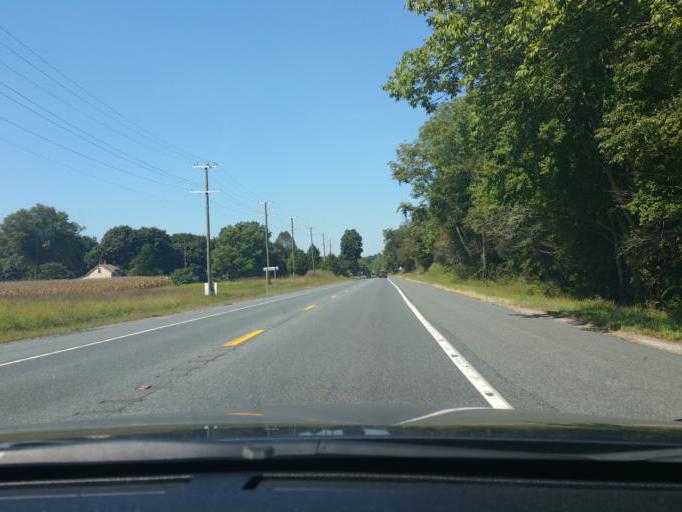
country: US
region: Maryland
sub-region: Harford County
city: Aberdeen
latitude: 39.5743
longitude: -76.1814
